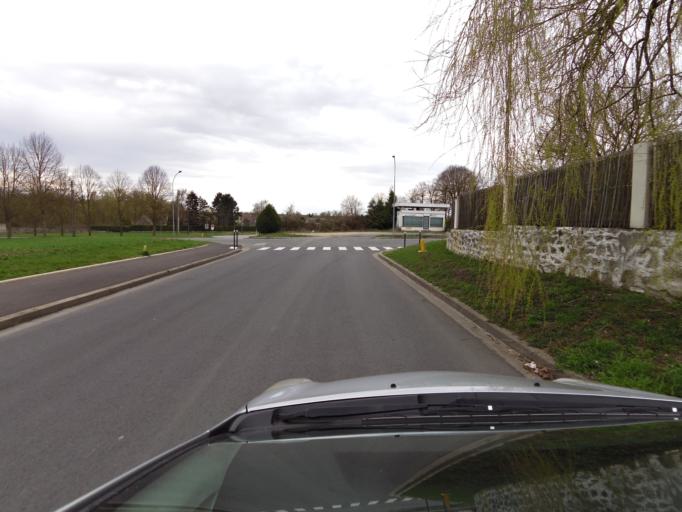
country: FR
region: Picardie
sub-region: Departement de l'Oise
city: Senlis
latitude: 49.2025
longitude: 2.5984
